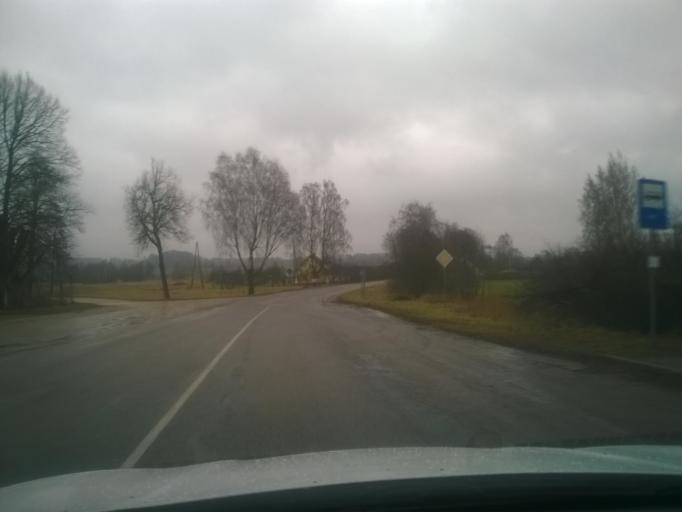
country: LV
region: Jaunpils
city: Jaunpils
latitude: 56.9096
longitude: 22.9676
